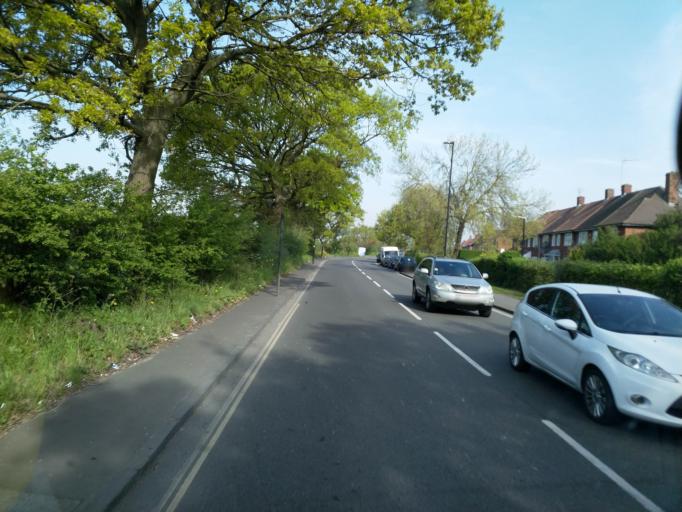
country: GB
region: England
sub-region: Greater London
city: Feltham
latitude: 51.4672
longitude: -0.4014
